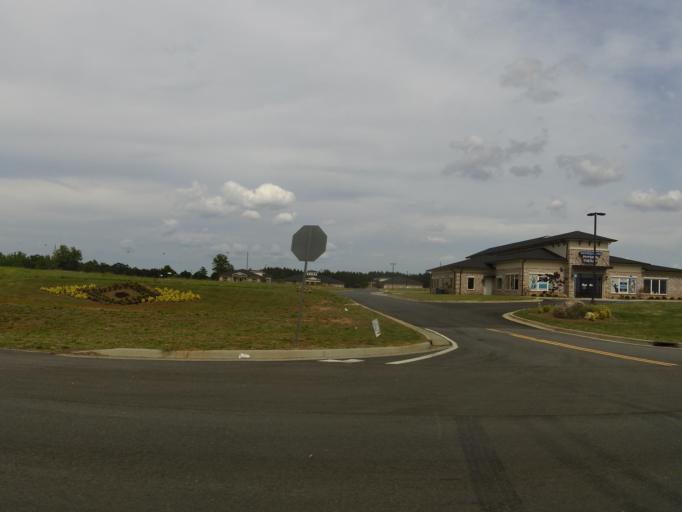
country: US
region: Georgia
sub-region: McDuffie County
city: Thomson
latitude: 33.5242
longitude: -82.5046
